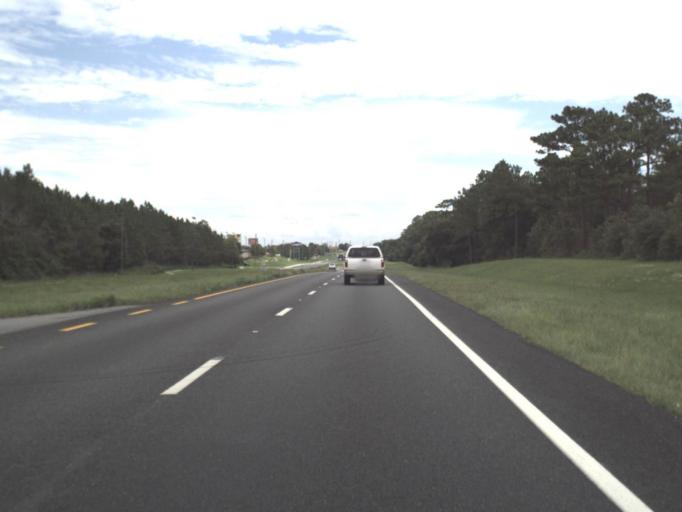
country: US
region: Florida
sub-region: Citrus County
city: Inverness Highlands North
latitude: 28.8558
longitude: -82.4024
